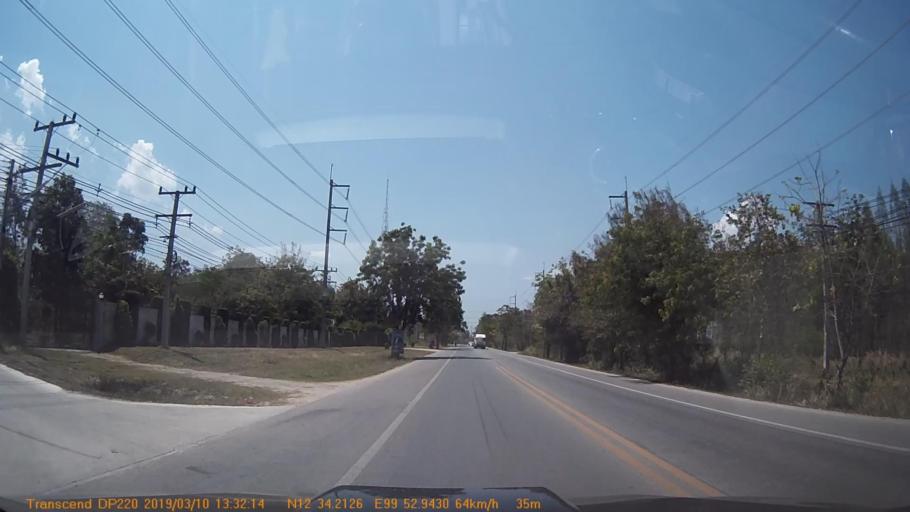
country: TH
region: Prachuap Khiri Khan
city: Hua Hin
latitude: 12.5703
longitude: 99.8822
